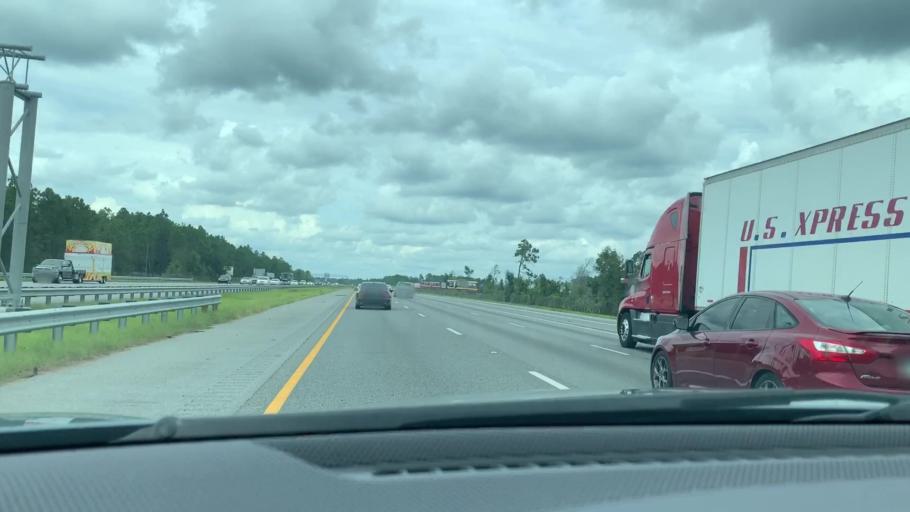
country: US
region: Georgia
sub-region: McIntosh County
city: Darien
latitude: 31.4011
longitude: -81.4473
